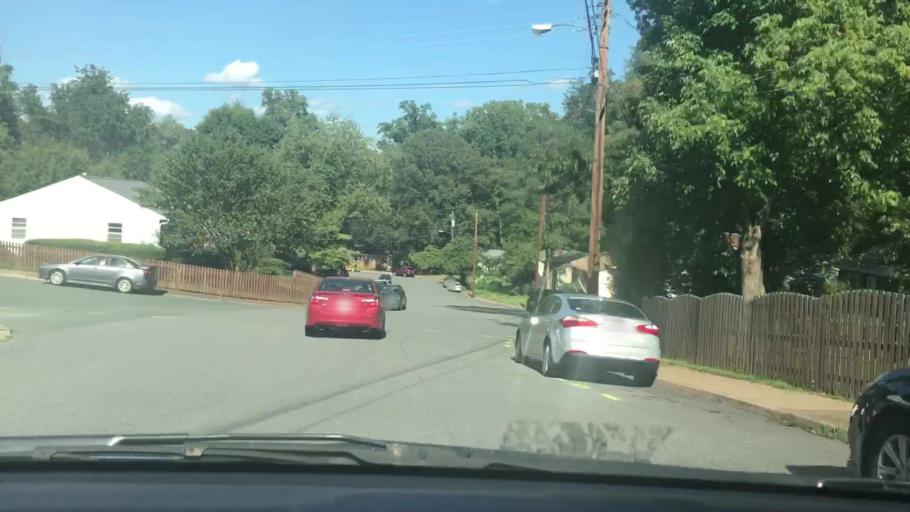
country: US
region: Virginia
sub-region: City of Charlottesville
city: Charlottesville
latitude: 38.0260
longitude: -78.5073
